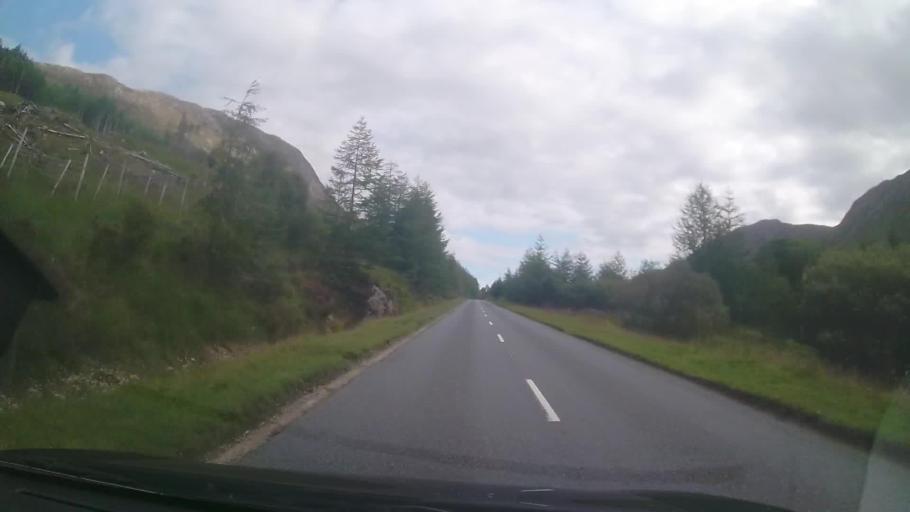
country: GB
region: Scotland
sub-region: Argyll and Bute
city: Oban
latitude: 56.6884
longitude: -5.4721
